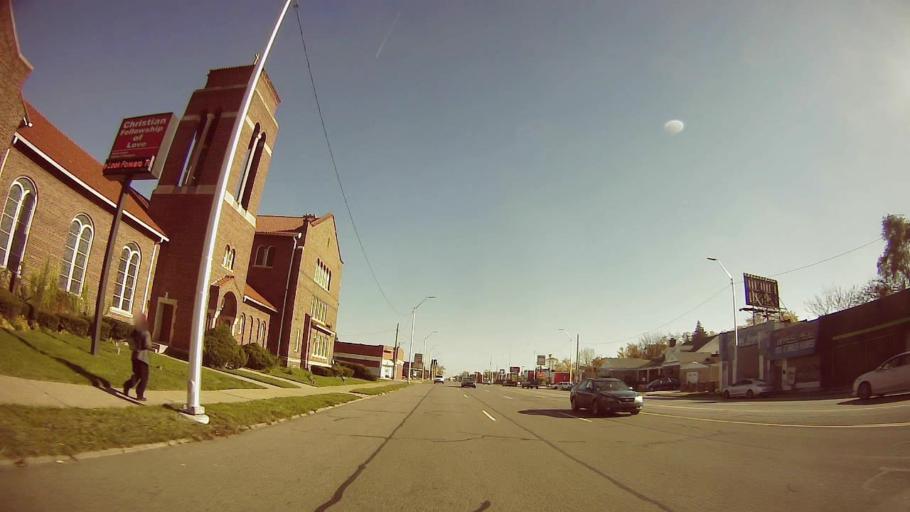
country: US
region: Michigan
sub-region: Wayne County
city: Redford
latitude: 42.4189
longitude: -83.2633
